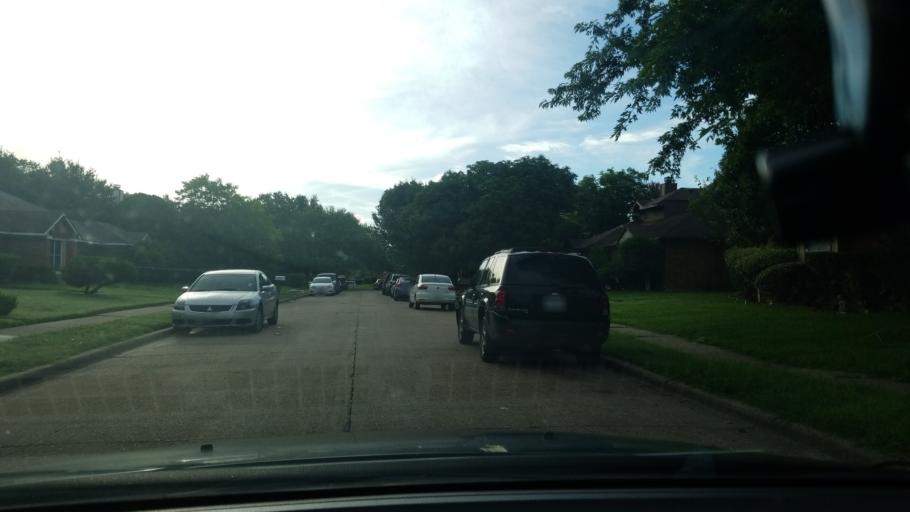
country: US
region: Texas
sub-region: Dallas County
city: Balch Springs
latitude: 32.7549
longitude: -96.6461
